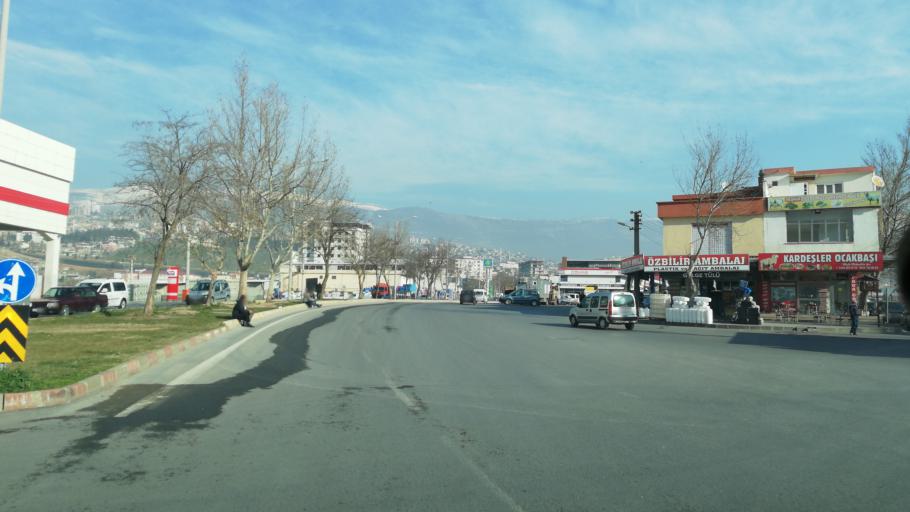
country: TR
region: Kahramanmaras
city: Kahramanmaras
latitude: 37.5656
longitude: 36.9170
